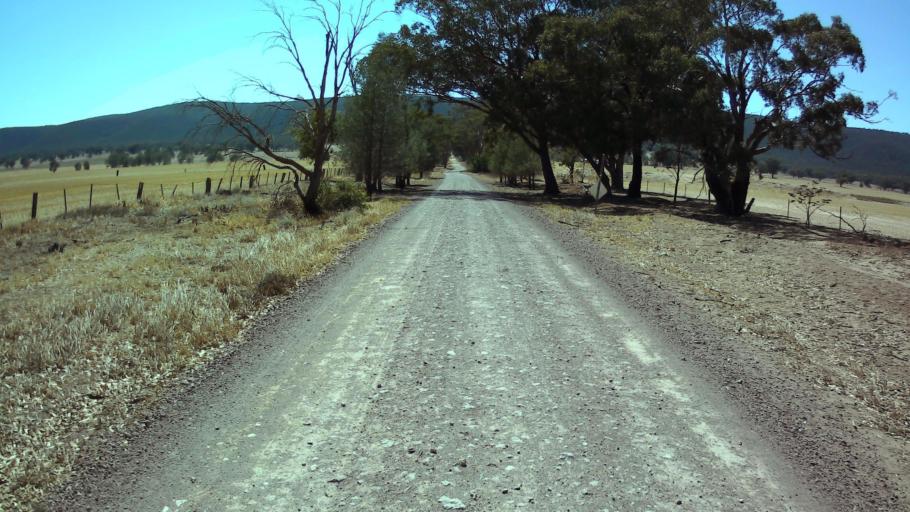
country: AU
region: New South Wales
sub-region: Weddin
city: Grenfell
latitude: -33.7027
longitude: 148.3287
